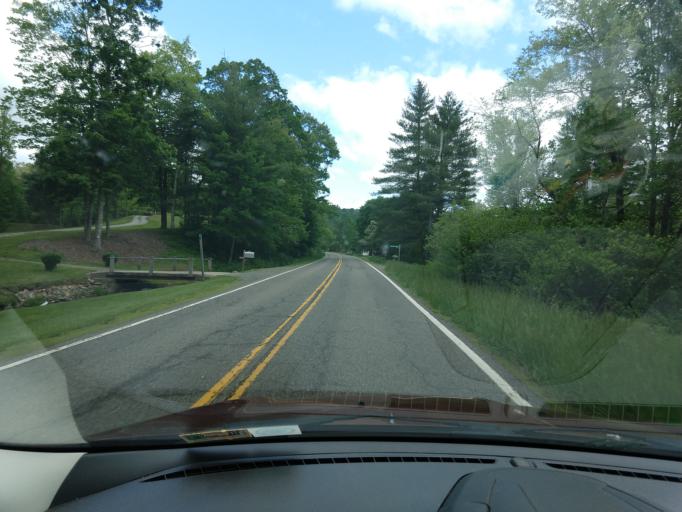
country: US
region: Virginia
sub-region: City of Galax
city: Galax
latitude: 36.7895
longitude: -80.9841
